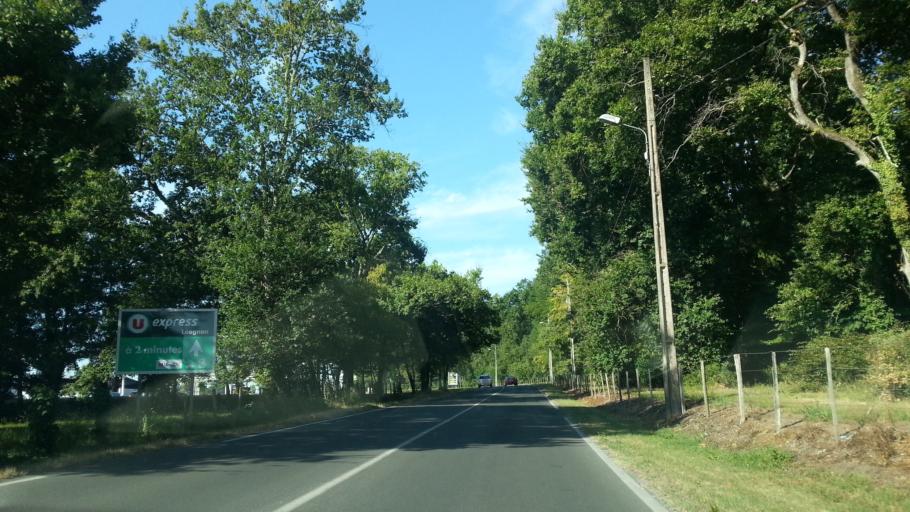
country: FR
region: Aquitaine
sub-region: Departement de la Gironde
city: Leognan
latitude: 44.7492
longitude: -0.5890
